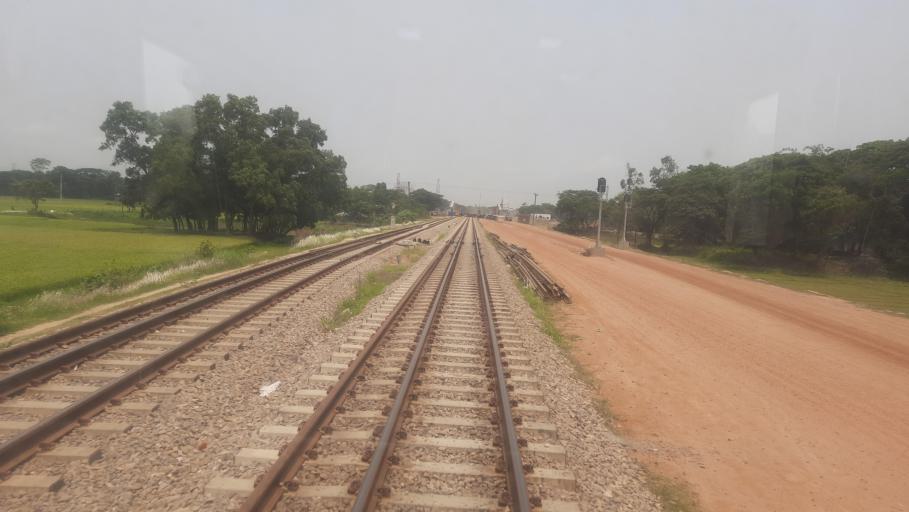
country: BD
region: Chittagong
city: Comilla
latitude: 23.6342
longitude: 91.1469
